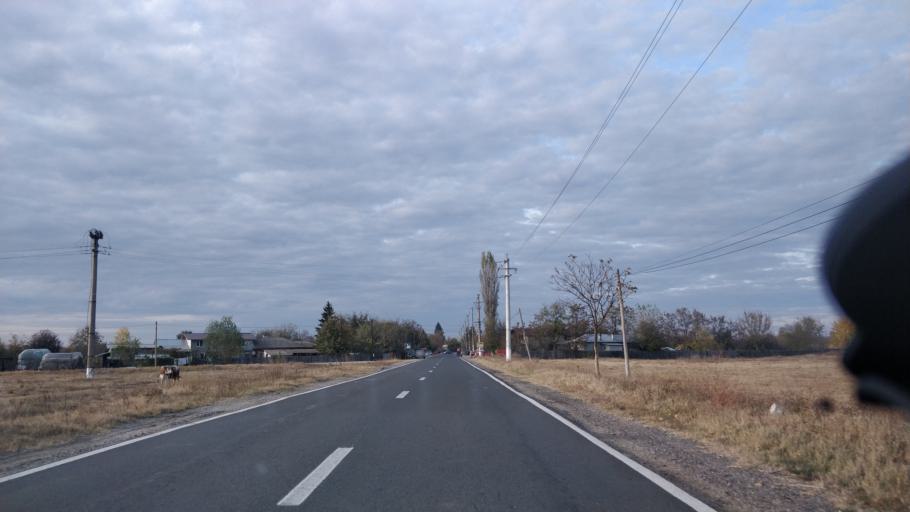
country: RO
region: Giurgiu
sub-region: Comuna Bucsani
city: Bucsani
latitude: 44.3589
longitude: 25.6690
